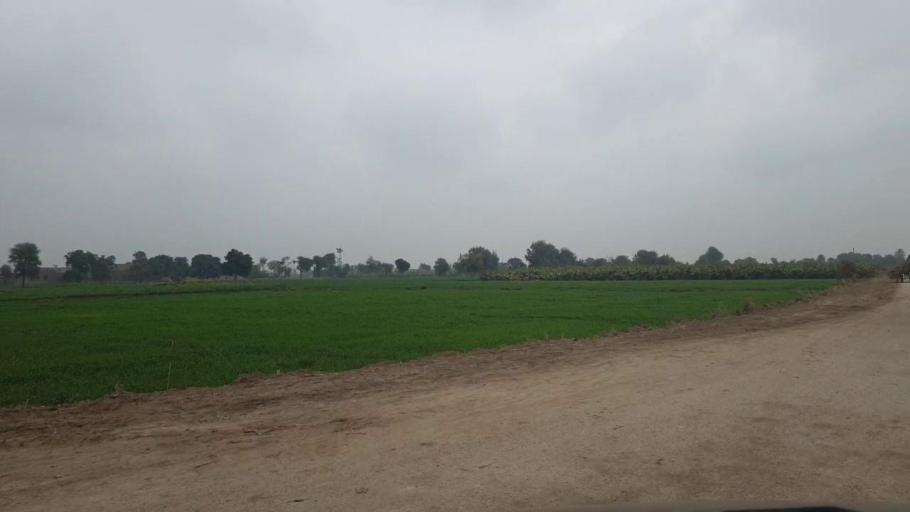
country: PK
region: Sindh
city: Shahdadpur
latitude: 25.8667
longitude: 68.6870
